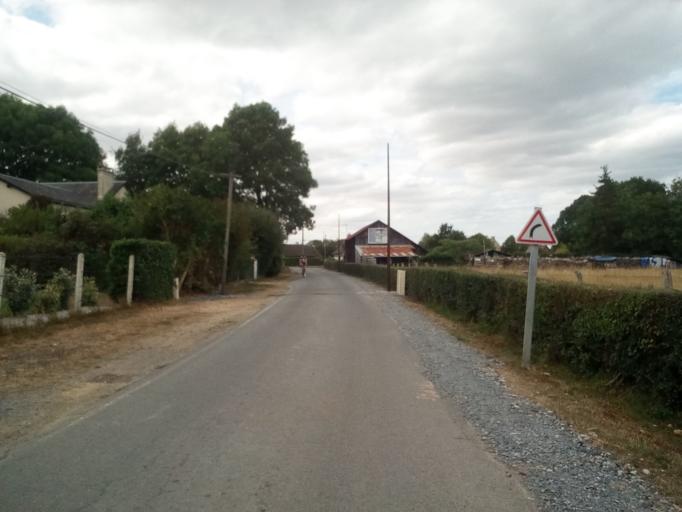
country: FR
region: Lower Normandy
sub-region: Departement du Calvados
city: Troarn
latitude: 49.1620
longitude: -0.1602
